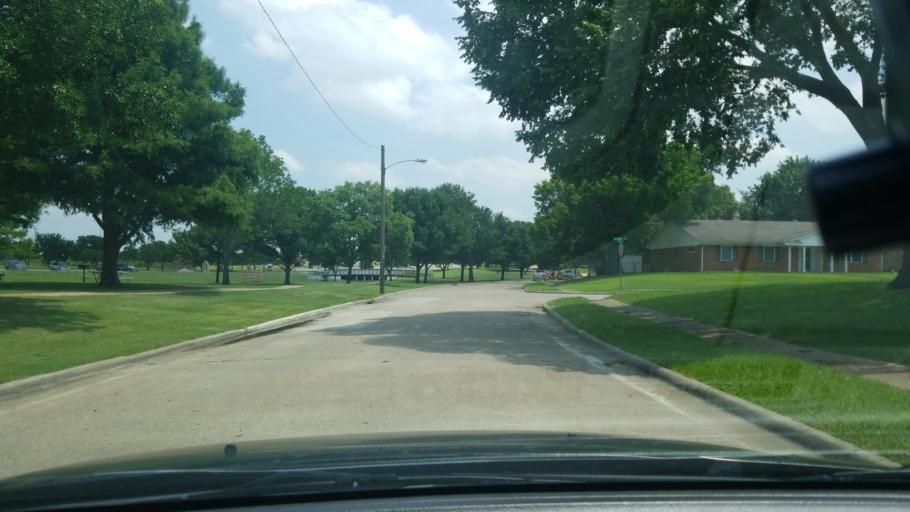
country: US
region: Texas
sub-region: Dallas County
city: Mesquite
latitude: 32.8034
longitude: -96.6355
